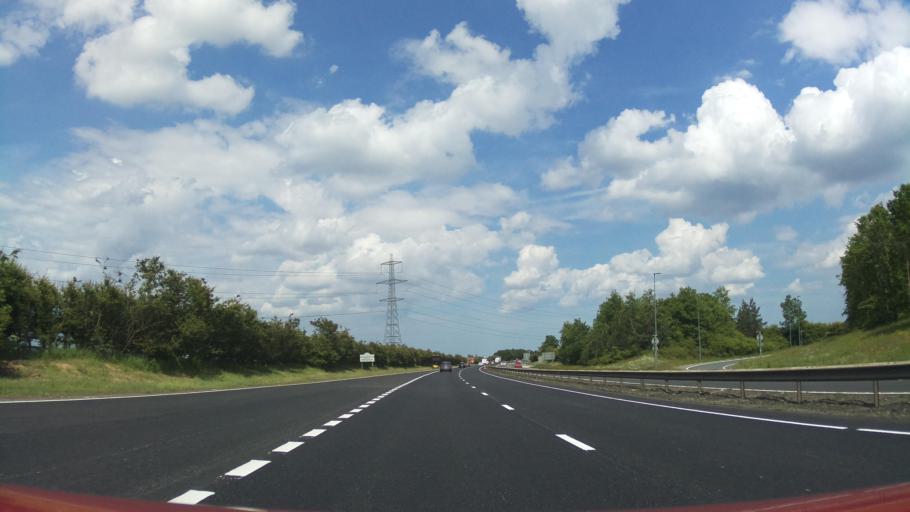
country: GB
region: England
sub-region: Stockton-on-Tees
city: Yarm
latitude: 54.4723
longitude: -1.3236
